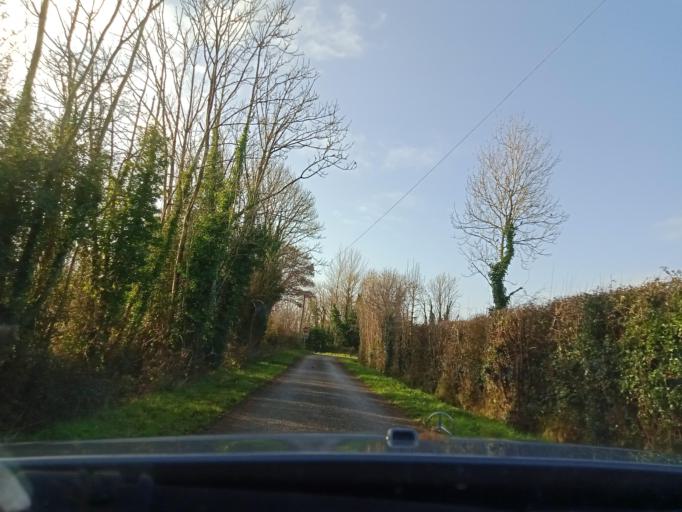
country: IE
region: Leinster
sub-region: Kilkenny
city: Callan
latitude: 52.5231
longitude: -7.3999
